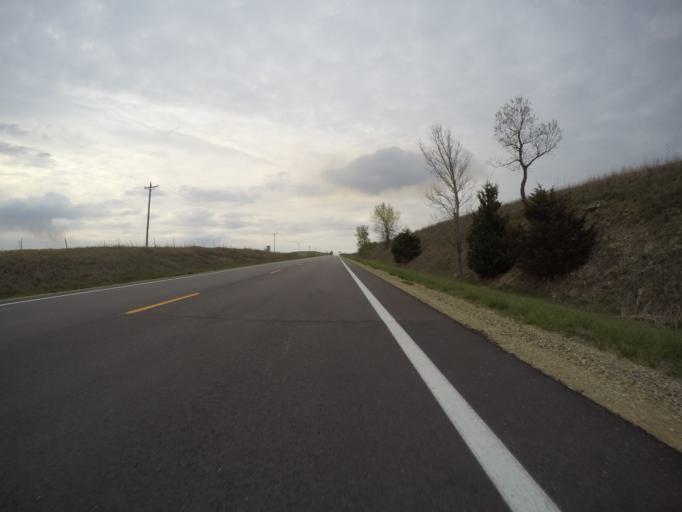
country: US
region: Kansas
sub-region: Pottawatomie County
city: Westmoreland
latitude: 39.3685
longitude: -96.5197
